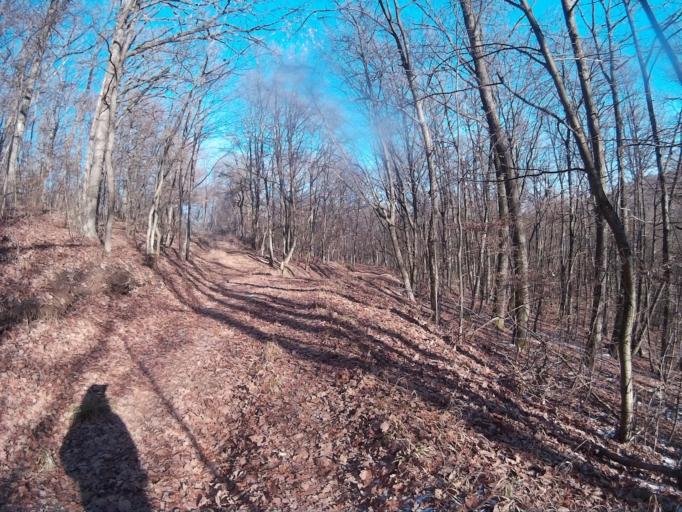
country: HU
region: Borsod-Abauj-Zemplen
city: Rudabanya
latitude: 48.4965
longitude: 20.5868
